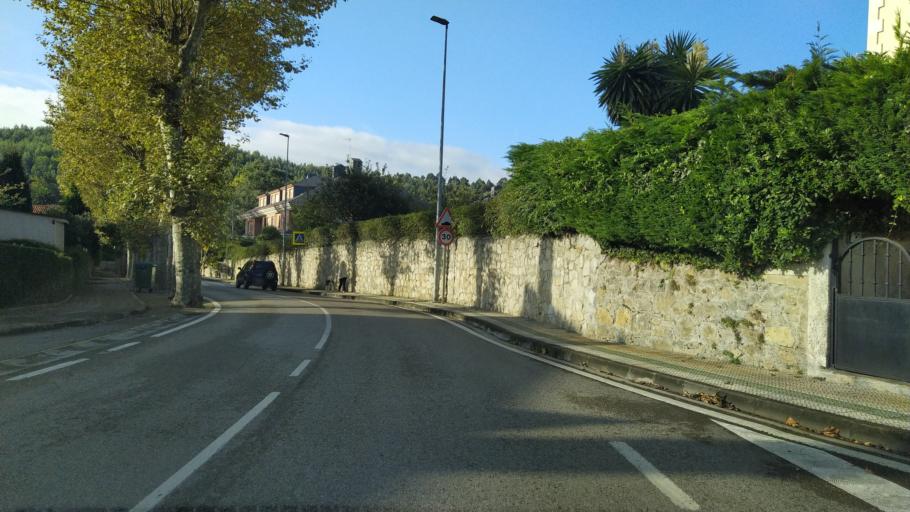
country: ES
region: Cantabria
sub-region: Provincia de Cantabria
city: Santa Cruz de Bezana
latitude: 43.4436
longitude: -3.9297
